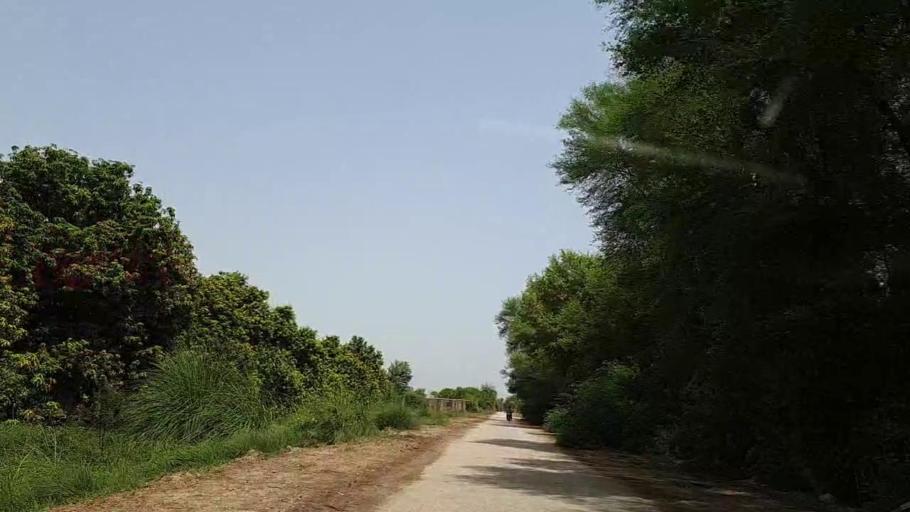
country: PK
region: Sindh
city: Tharu Shah
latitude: 26.9541
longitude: 68.0264
